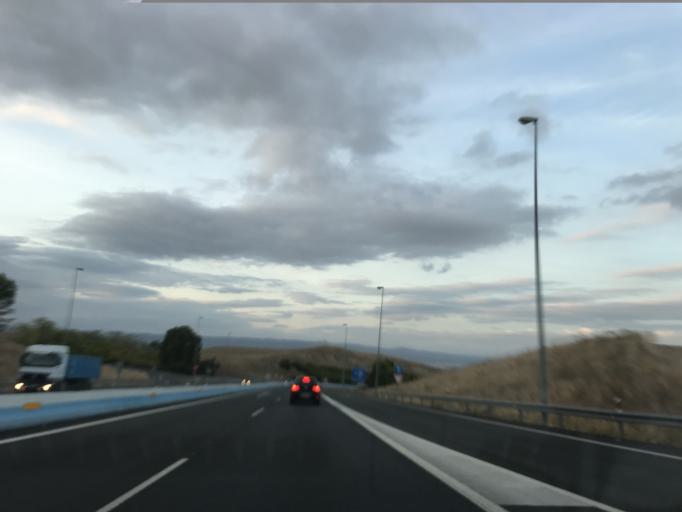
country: ES
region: Andalusia
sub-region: Province of Cordoba
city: La Victoria
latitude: 37.7630
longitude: -4.8224
